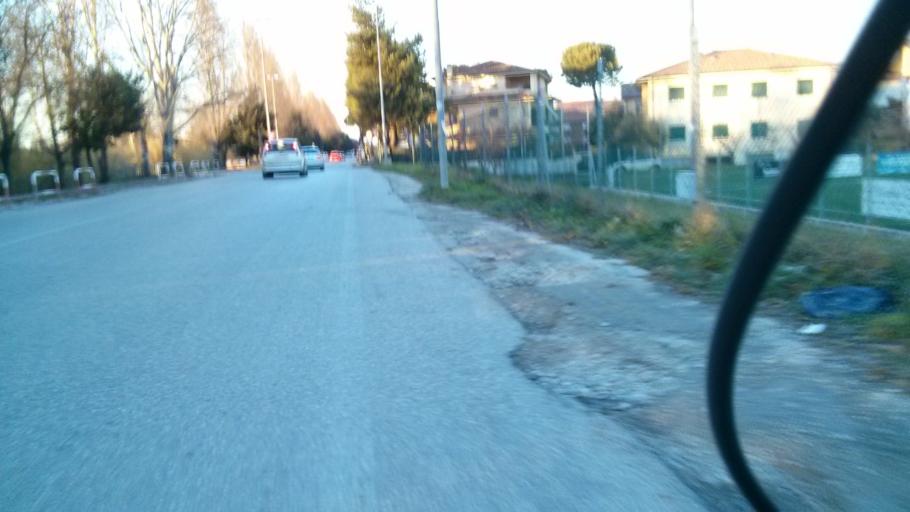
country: IT
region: The Marches
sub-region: Provincia di Pesaro e Urbino
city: Fano
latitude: 43.8310
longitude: 13.0146
